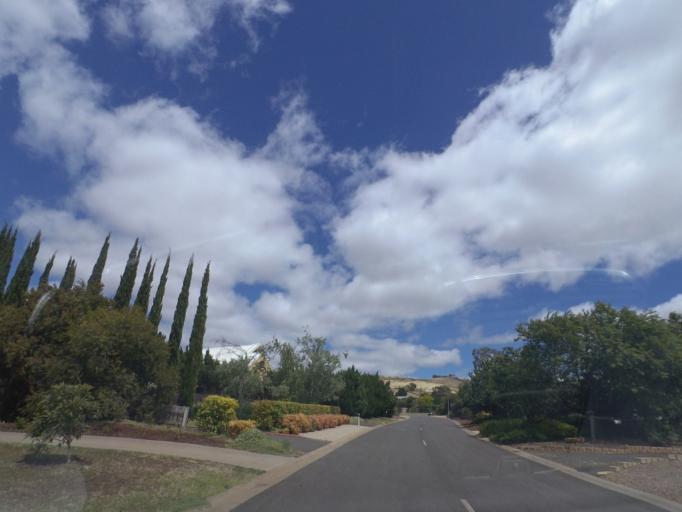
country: AU
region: Victoria
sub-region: Moorabool
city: Bacchus Marsh
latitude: -37.6357
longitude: 144.4224
